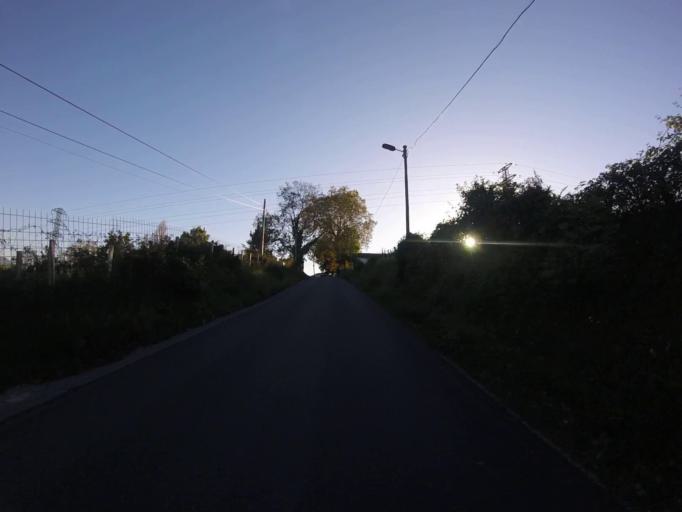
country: ES
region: Basque Country
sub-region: Provincia de Guipuzcoa
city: Lasarte
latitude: 43.2967
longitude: -2.0137
